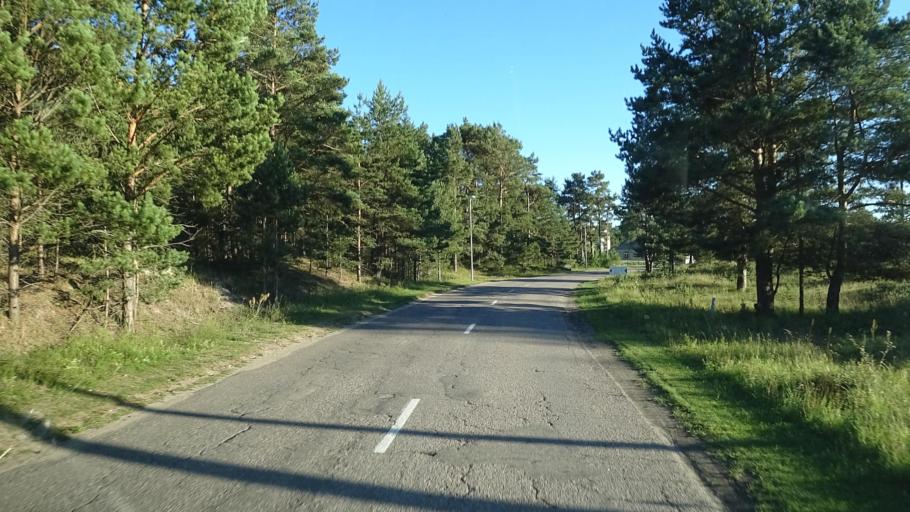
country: LV
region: Rojas
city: Roja
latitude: 57.7476
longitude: 22.5925
